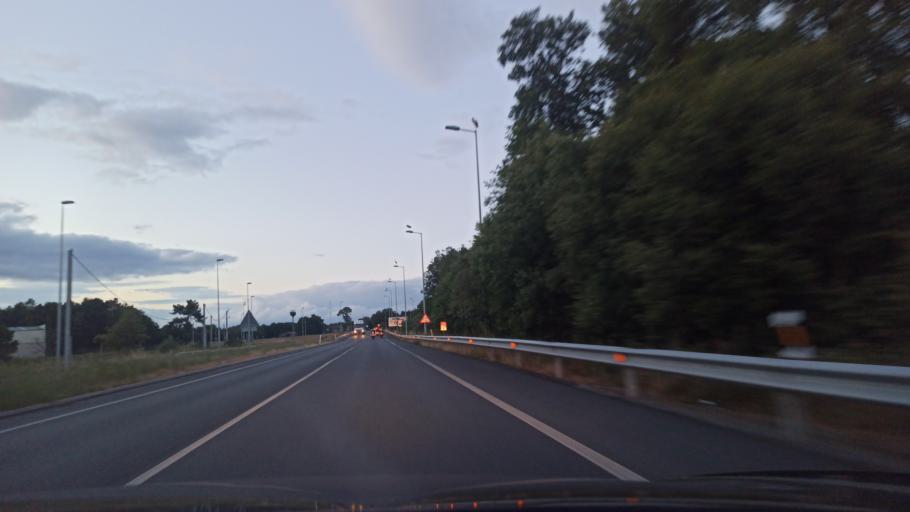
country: ES
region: Galicia
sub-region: Provincia de Lugo
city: Lugo
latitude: 42.9782
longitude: -7.5882
